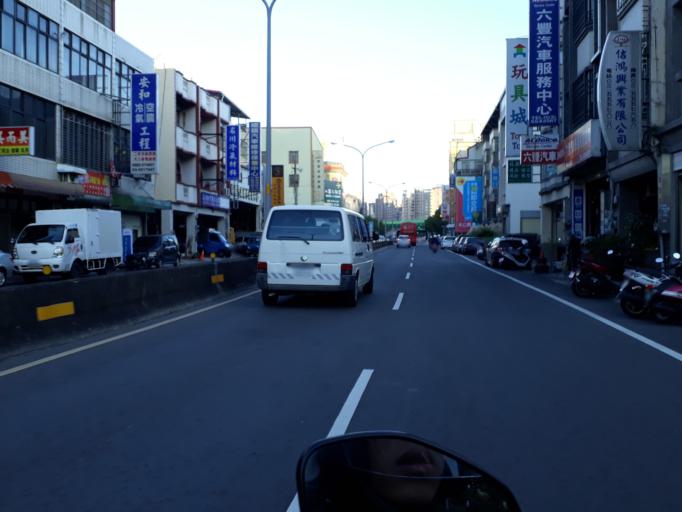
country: TW
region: Taiwan
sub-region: Hsinchu
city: Zhubei
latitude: 24.8223
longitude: 121.0117
